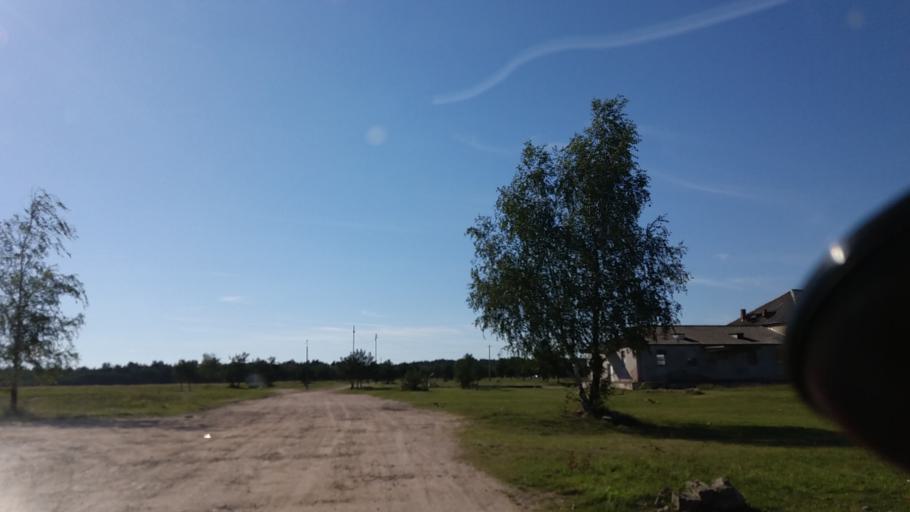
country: PL
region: West Pomeranian Voivodeship
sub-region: Powiat szczecinecki
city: Borne Sulinowo
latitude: 53.5778
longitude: 16.5302
